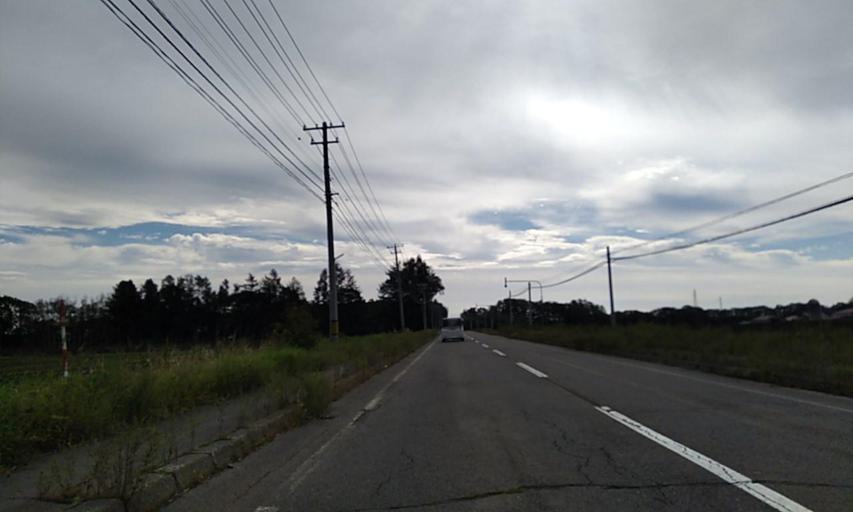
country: JP
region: Hokkaido
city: Obihiro
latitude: 42.8480
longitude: 143.1690
